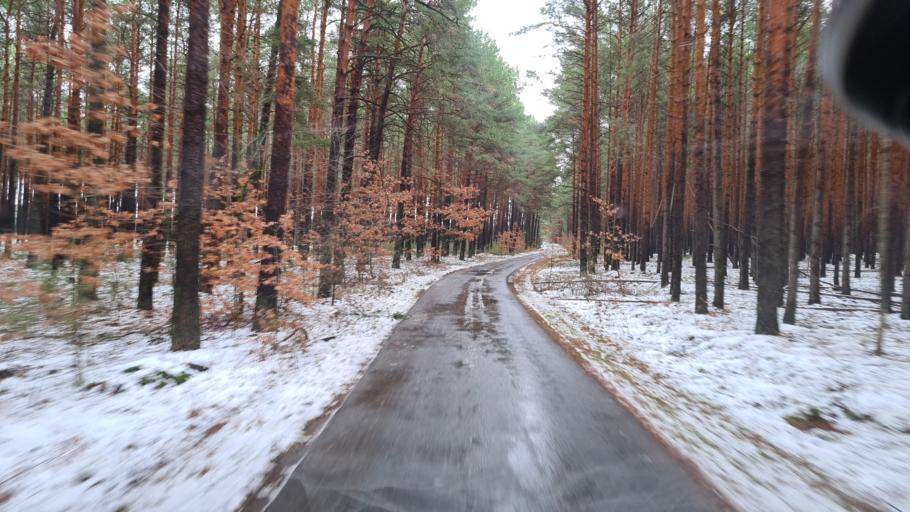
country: DE
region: Brandenburg
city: Janschwalde
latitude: 51.9014
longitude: 14.5313
